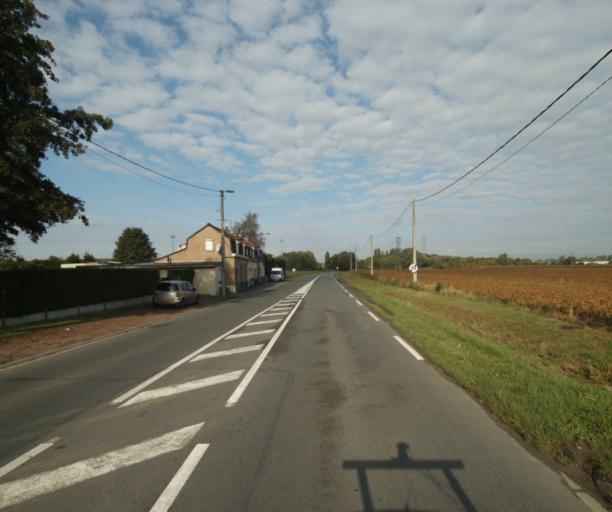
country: FR
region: Nord-Pas-de-Calais
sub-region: Departement du Nord
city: Lompret
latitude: 50.6565
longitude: 2.9966
